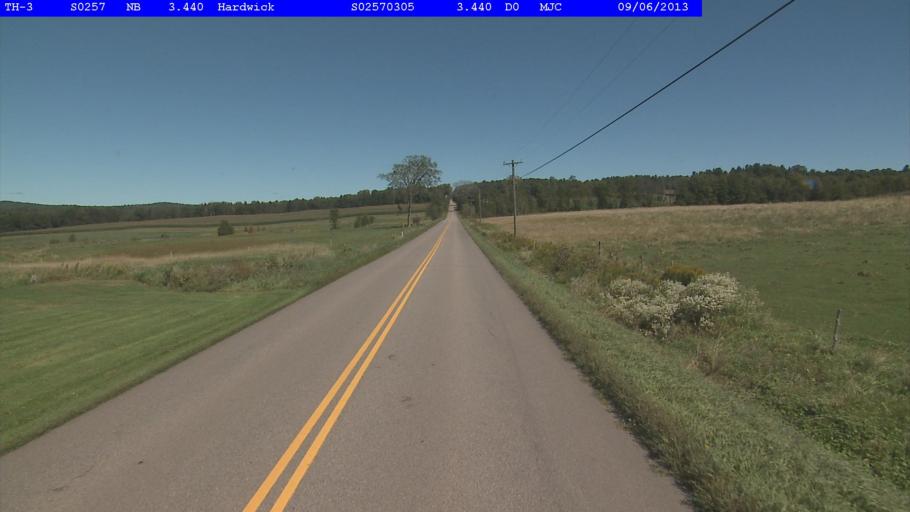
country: US
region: Vermont
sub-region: Caledonia County
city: Hardwick
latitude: 44.5387
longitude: -72.3292
